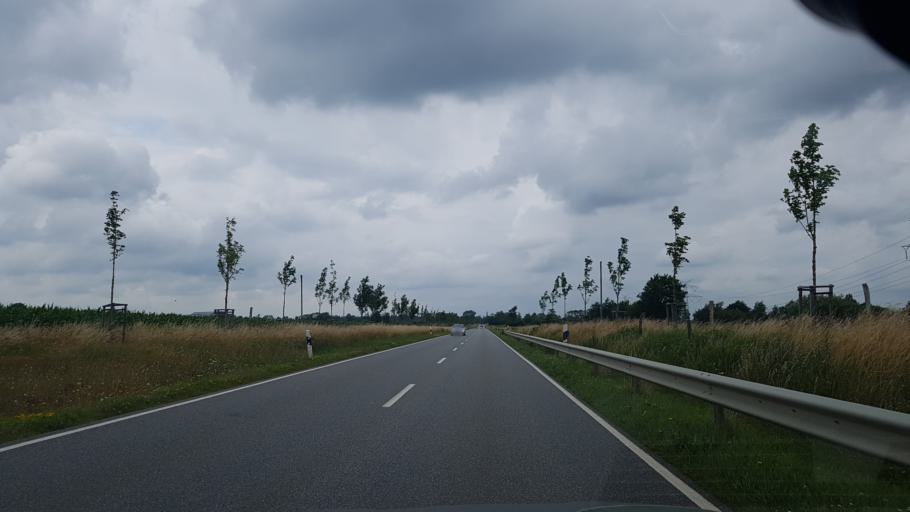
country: DE
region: Schleswig-Holstein
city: Osterby
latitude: 54.8095
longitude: 9.2349
